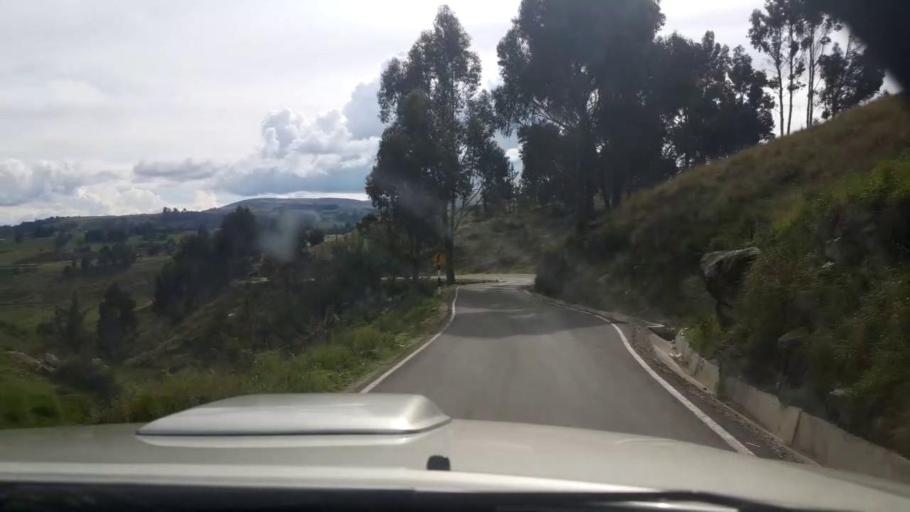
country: PE
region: Ayacucho
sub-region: Provincia de Cangallo
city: Pampa Cangallo
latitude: -13.4484
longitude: -74.1972
